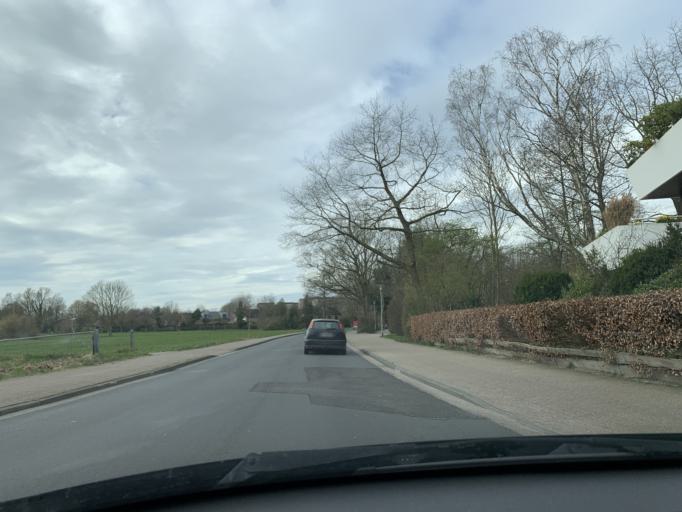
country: DE
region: Lower Saxony
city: Oldenburg
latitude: 53.1284
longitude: 8.1898
